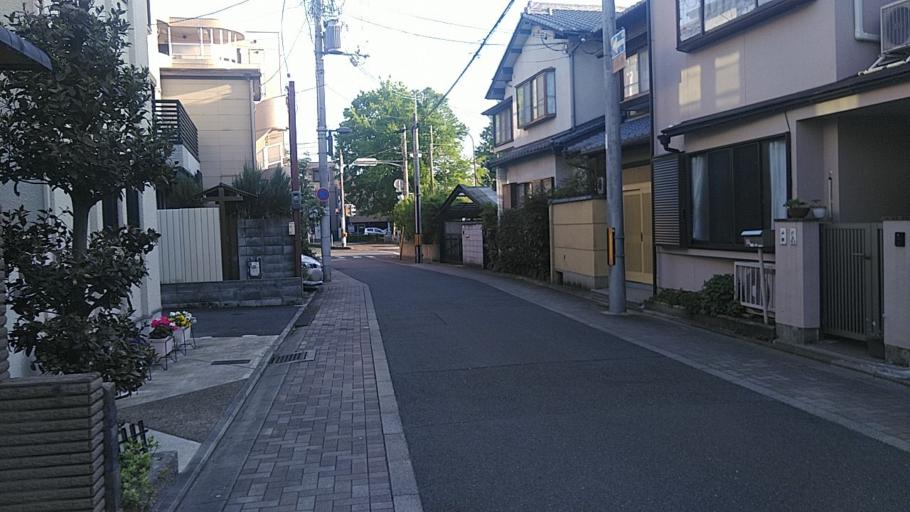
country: JP
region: Kyoto
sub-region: Kyoto-shi
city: Kamigyo-ku
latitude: 35.0403
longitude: 135.7573
